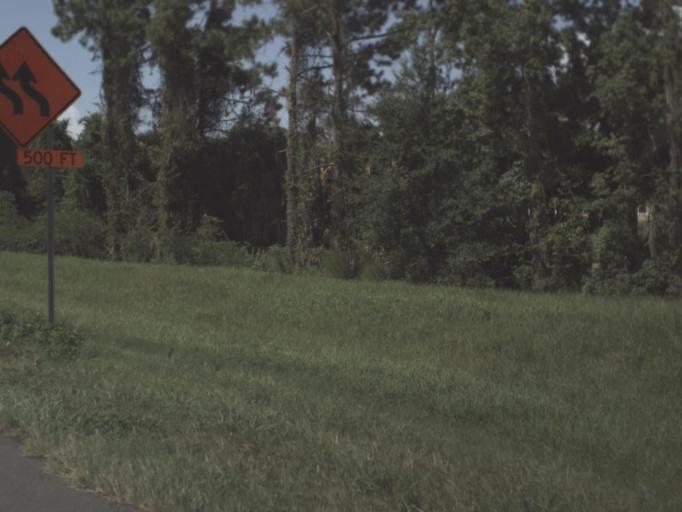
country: US
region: Florida
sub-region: Hillsborough County
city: Pebble Creek
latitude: 28.1594
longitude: -82.3934
